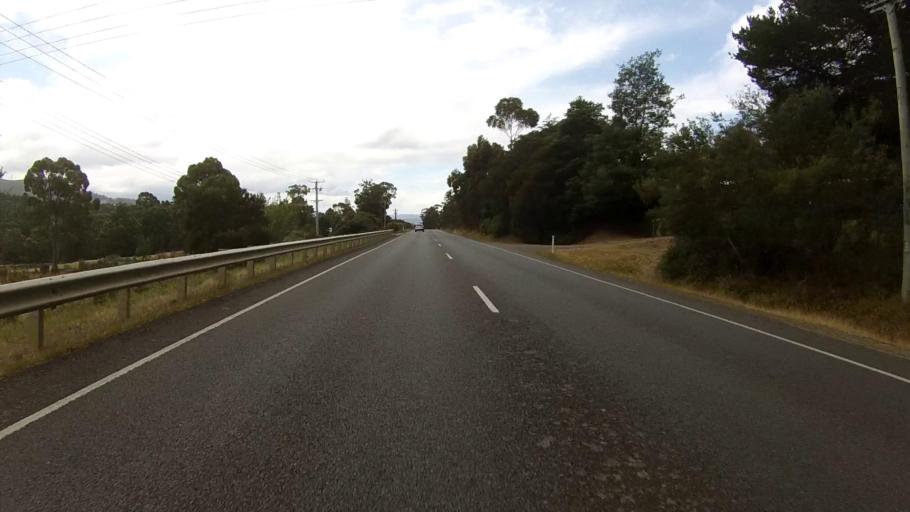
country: AU
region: Tasmania
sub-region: Kingborough
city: Kettering
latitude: -43.0823
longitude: 147.2539
